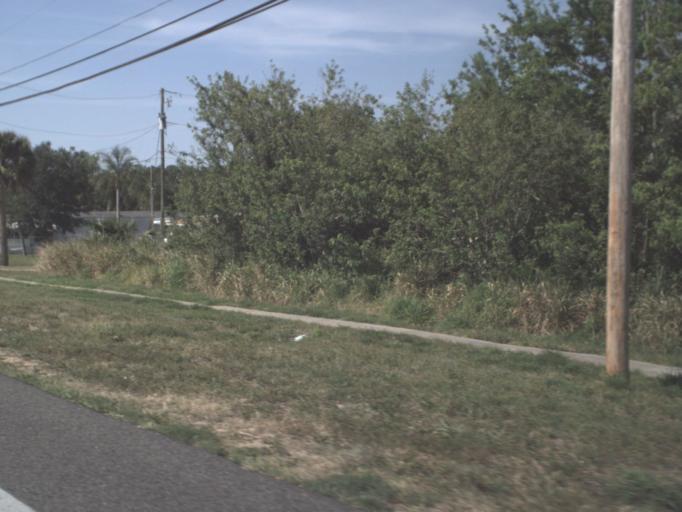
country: US
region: Florida
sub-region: Brevard County
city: Sharpes
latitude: 28.4340
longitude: -80.7605
